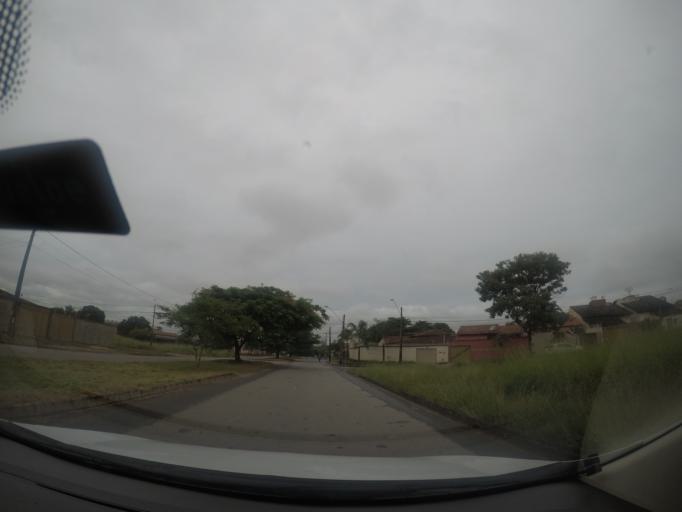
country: BR
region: Goias
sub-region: Goiania
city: Goiania
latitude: -16.7436
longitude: -49.3279
